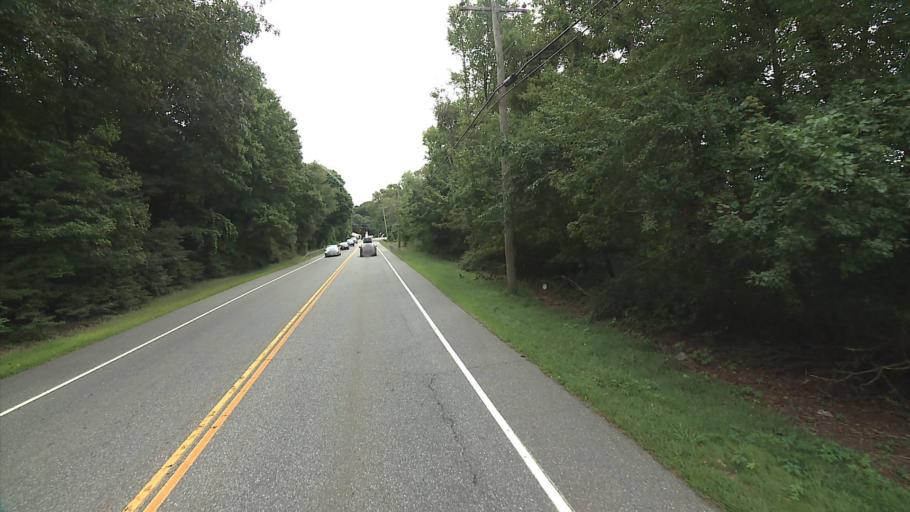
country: US
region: Connecticut
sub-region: Middlesex County
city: Old Saybrook Center
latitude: 41.2966
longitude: -72.3192
